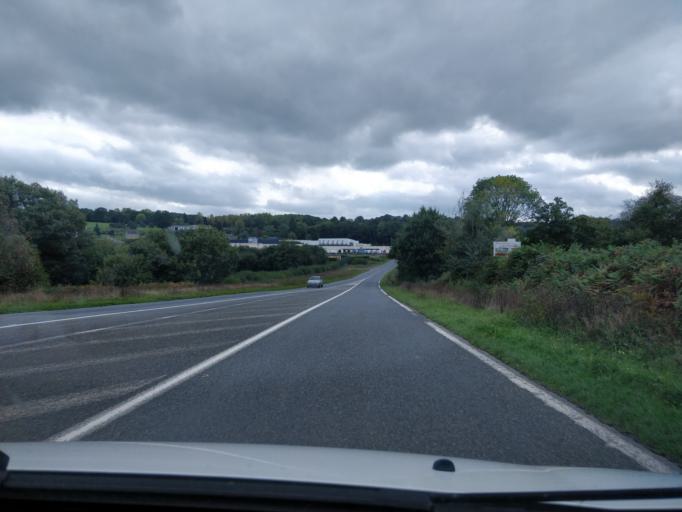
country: FR
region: Lower Normandy
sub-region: Departement de la Manche
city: Villedieu-les-Poeles
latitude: 48.8392
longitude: -1.2016
